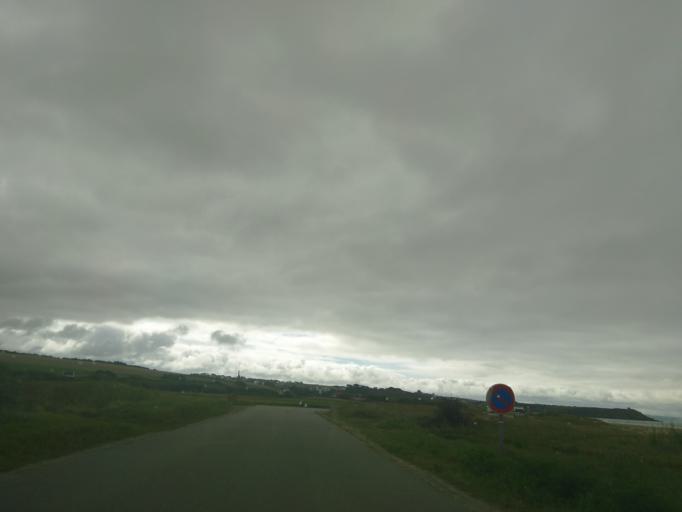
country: FR
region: Brittany
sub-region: Departement du Finistere
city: Plomodiern
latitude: 48.1844
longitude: -4.2948
